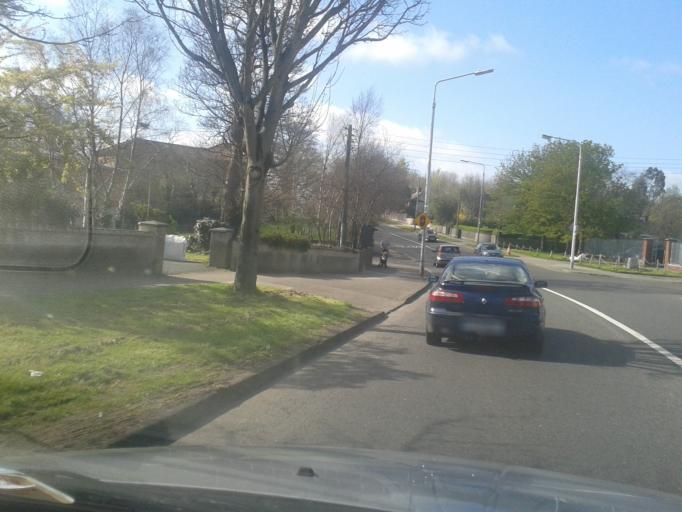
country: IE
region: Leinster
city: Raheny
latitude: 53.3871
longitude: -6.1741
